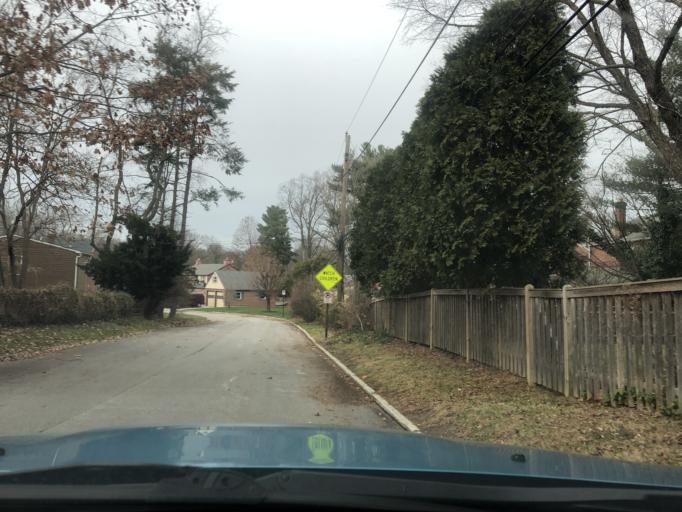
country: US
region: Pennsylvania
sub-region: Delaware County
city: Radnor
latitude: 40.0278
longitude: -75.3395
